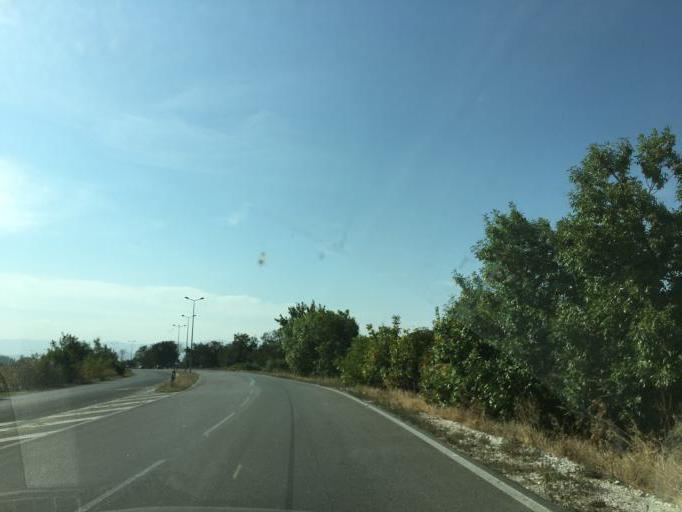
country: BG
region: Pazardzhik
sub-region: Obshtina Pazardzhik
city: Pazardzhik
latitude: 42.2239
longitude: 24.3102
